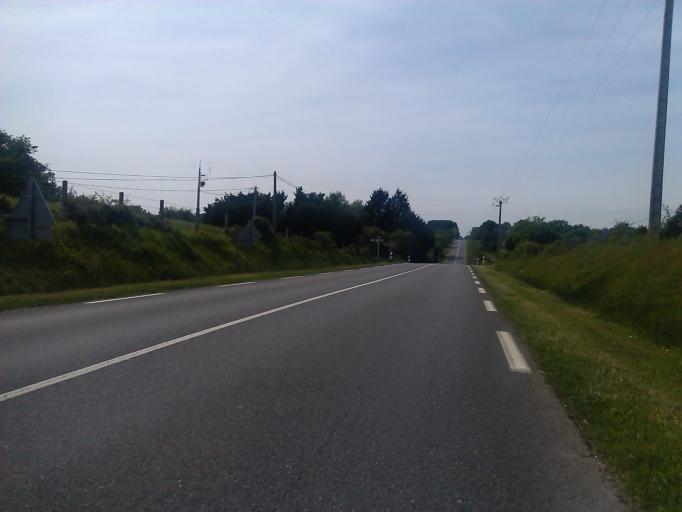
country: FR
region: Centre
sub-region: Departement du Cher
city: Chateaumeillant
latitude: 46.5528
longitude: 2.0933
